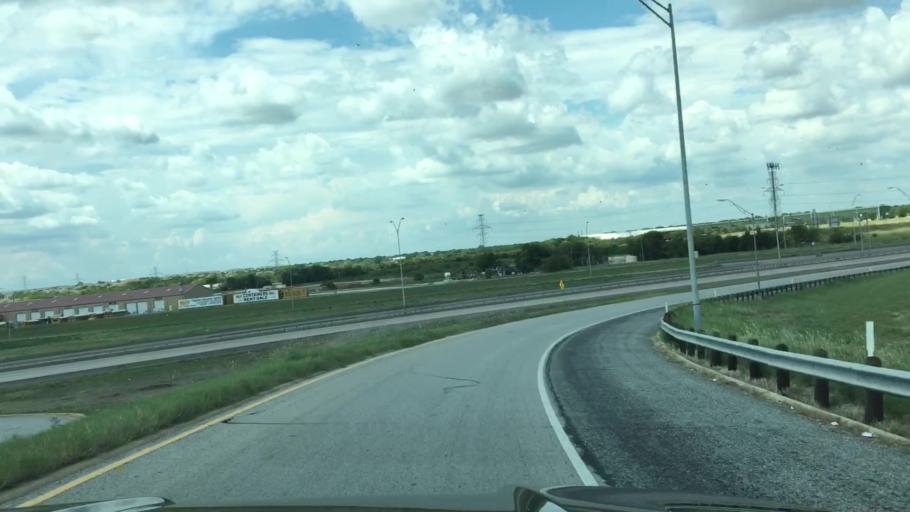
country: US
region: Texas
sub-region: Tarrant County
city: Saginaw
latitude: 32.8384
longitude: -97.3614
